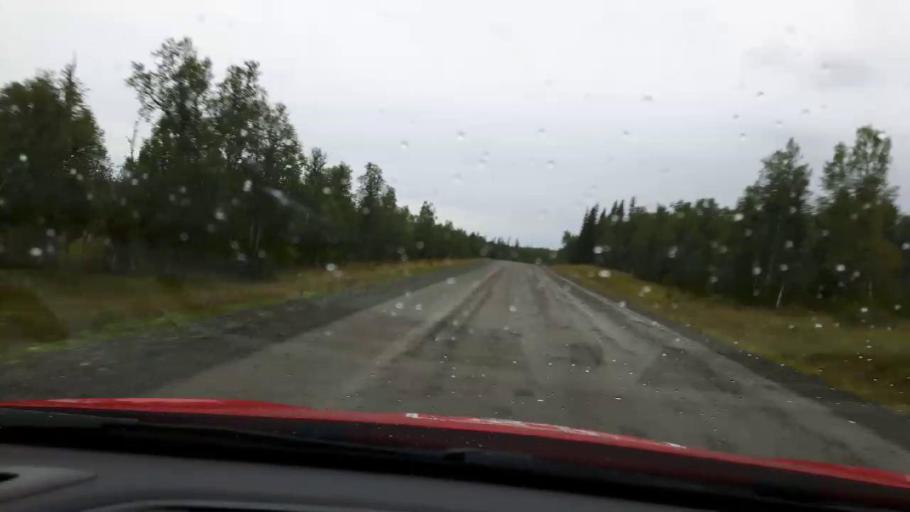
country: NO
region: Nord-Trondelag
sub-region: Meraker
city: Meraker
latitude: 63.5629
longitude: 12.2903
